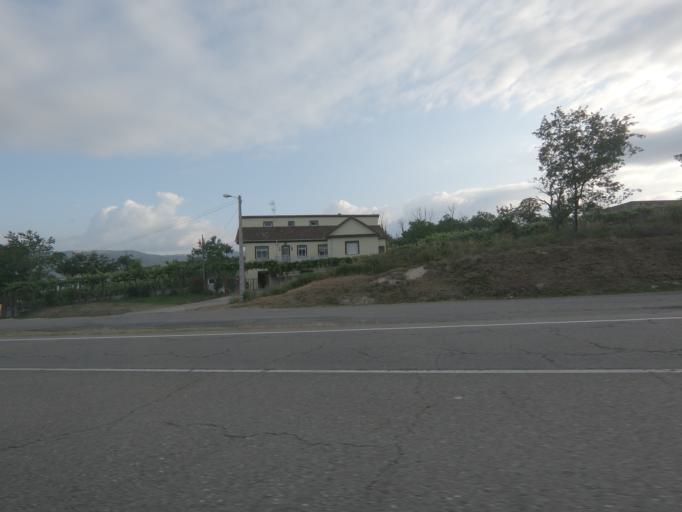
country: ES
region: Galicia
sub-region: Provincia de Ourense
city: Allariz
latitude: 42.2126
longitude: -7.8215
